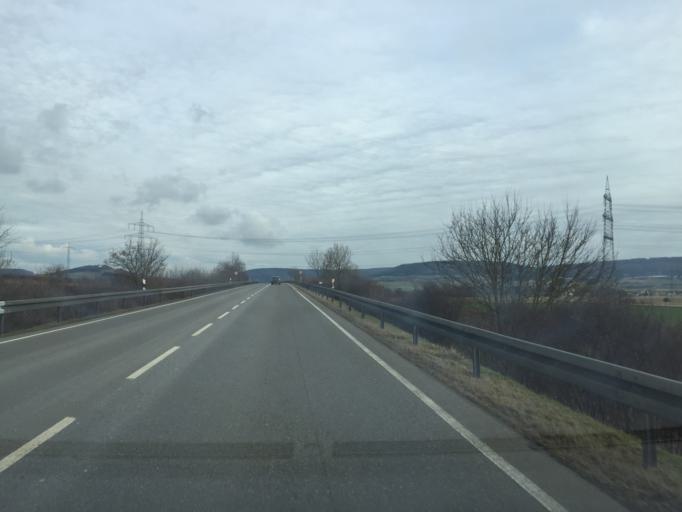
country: DE
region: Baden-Wuerttemberg
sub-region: Freiburg Region
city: Donaueschingen
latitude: 47.9272
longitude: 8.5499
